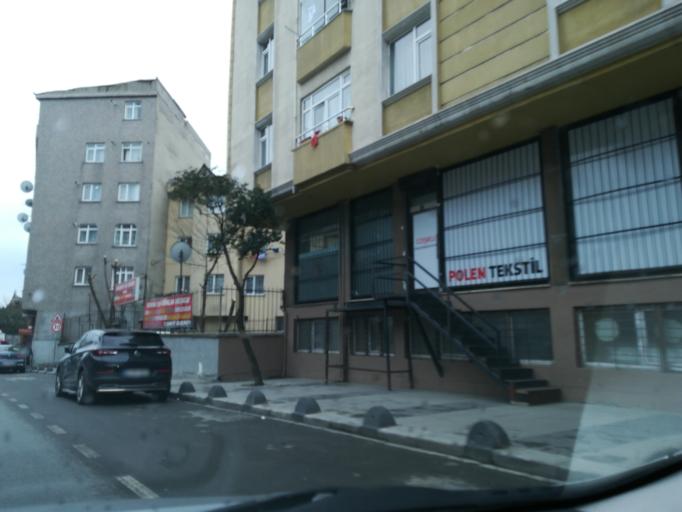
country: TR
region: Istanbul
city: Bagcilar
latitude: 41.0374
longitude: 28.8417
